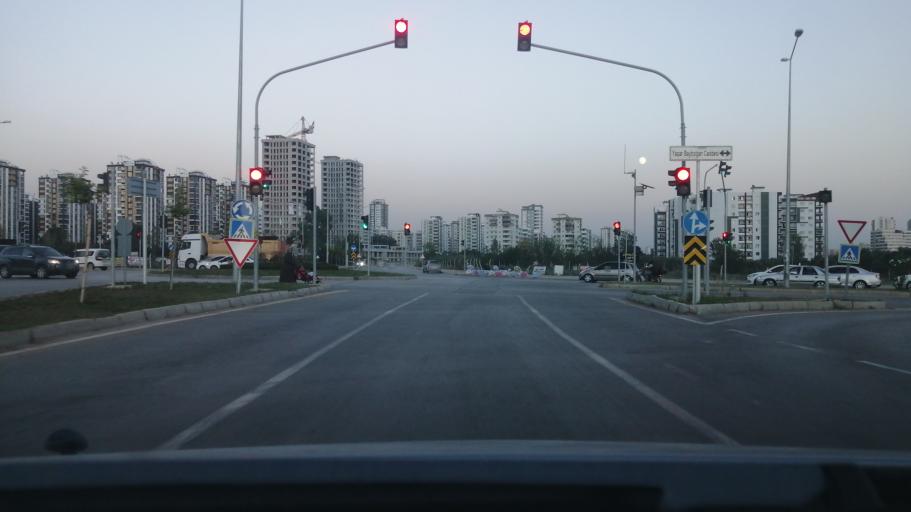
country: TR
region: Adana
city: Seyhan
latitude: 37.0153
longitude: 35.2571
